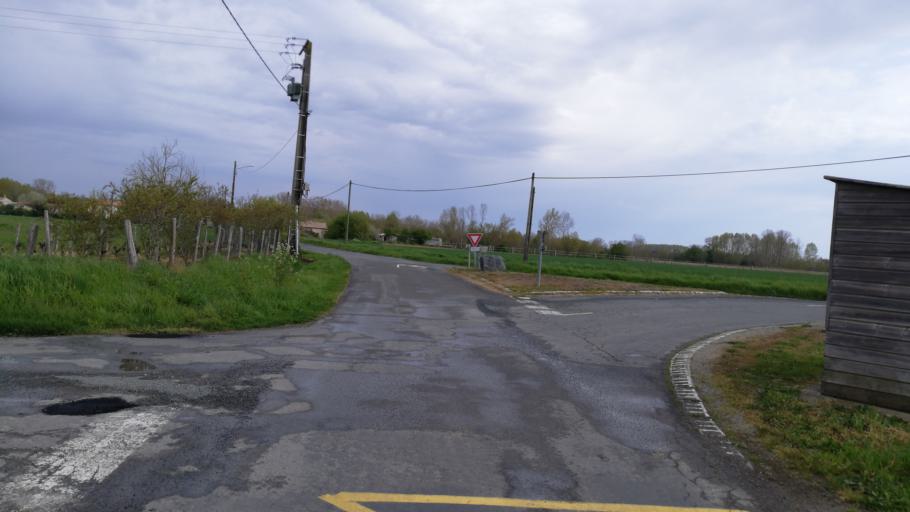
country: FR
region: Pays de la Loire
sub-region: Departement de la Vendee
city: Maillezais
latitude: 46.3313
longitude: -0.7099
